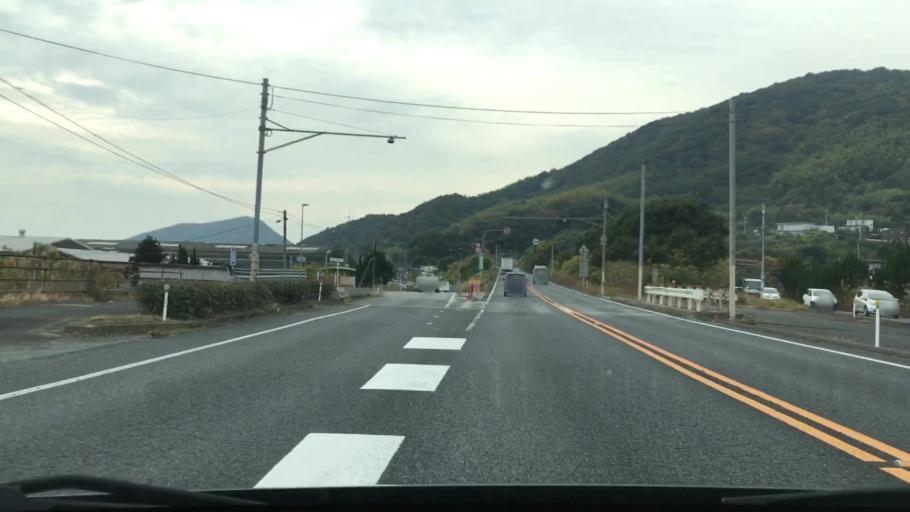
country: JP
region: Yamaguchi
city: Hofu
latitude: 34.0507
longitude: 131.6412
